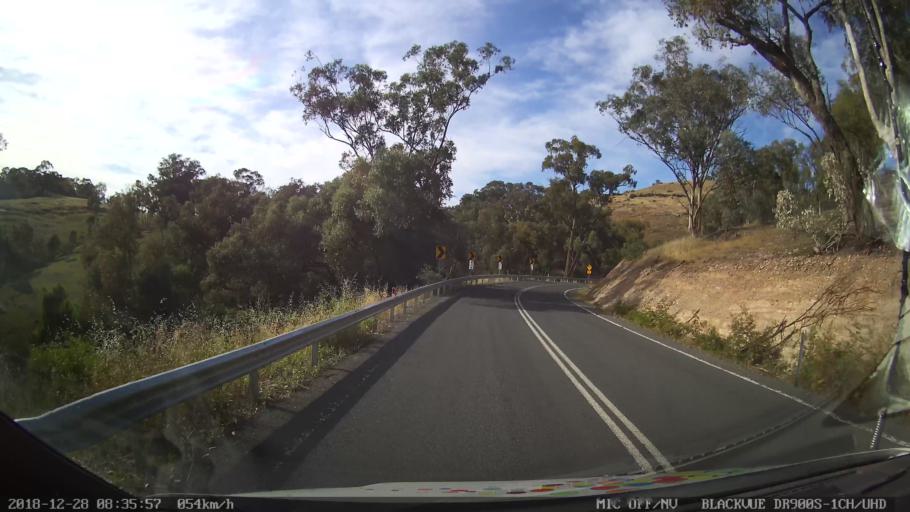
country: AU
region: New South Wales
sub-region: Blayney
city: Blayney
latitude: -33.9866
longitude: 149.3106
